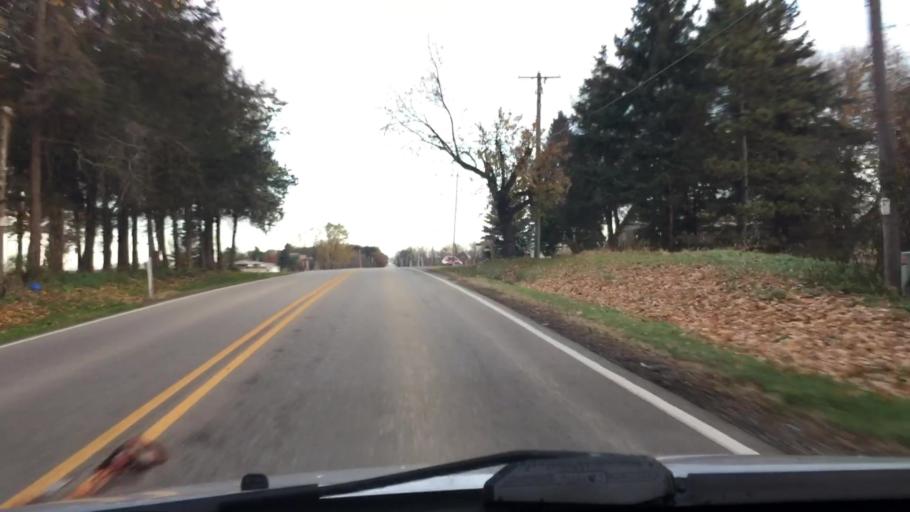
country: US
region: Wisconsin
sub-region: Waukesha County
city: Okauchee Lake
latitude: 43.1837
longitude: -88.4585
